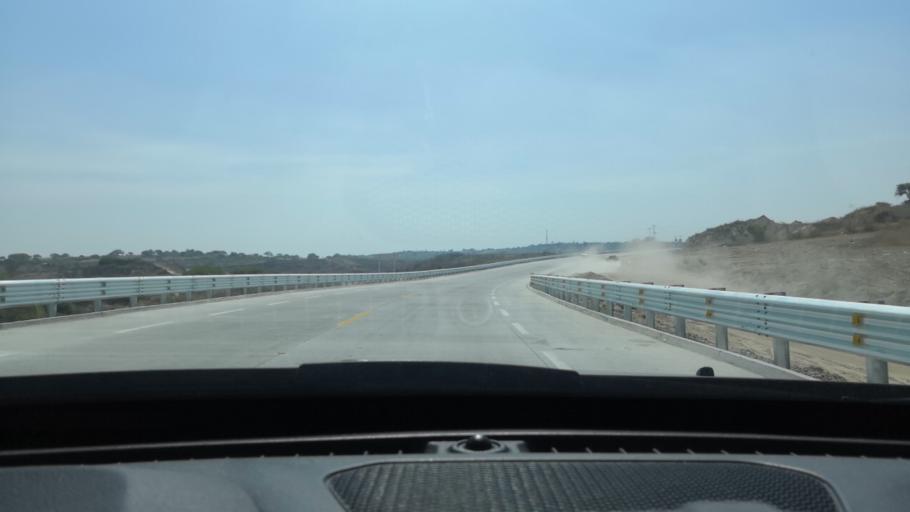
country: MX
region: Guanajuato
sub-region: Purisima del Rincon
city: Potrerillos (Guanajal)
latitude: 21.0659
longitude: -101.8723
